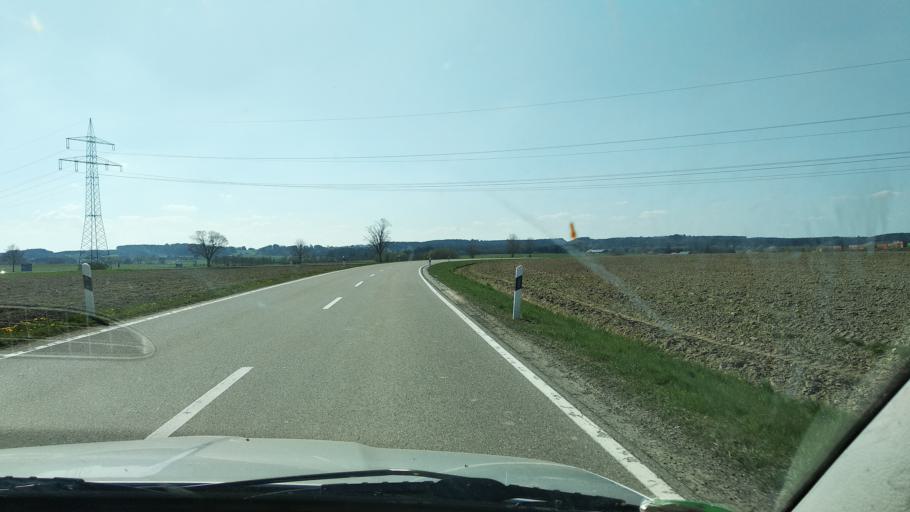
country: DE
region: Bavaria
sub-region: Swabia
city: Stetten
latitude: 48.0343
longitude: 10.4371
